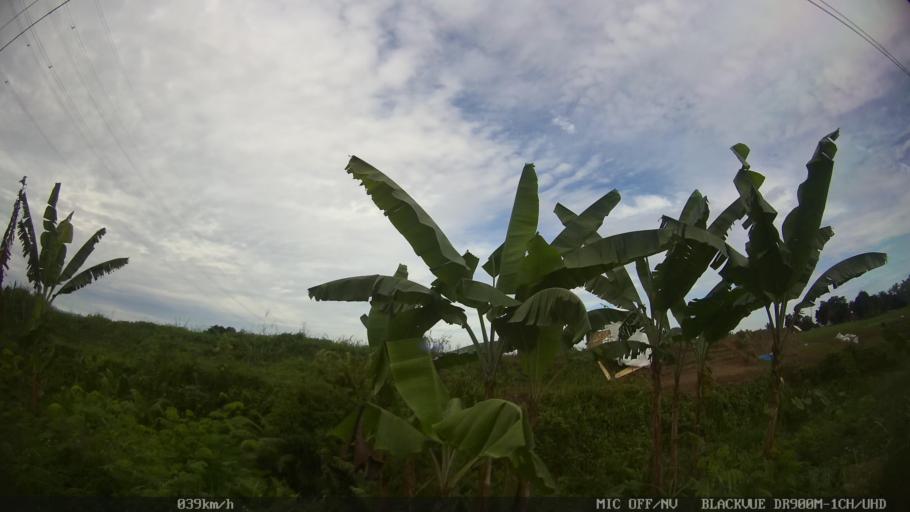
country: ID
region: North Sumatra
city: Sunggal
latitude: 3.5857
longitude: 98.5652
